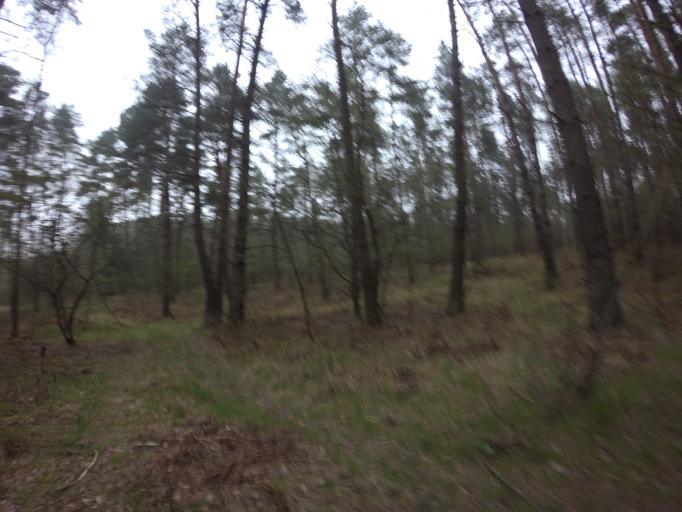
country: PL
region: West Pomeranian Voivodeship
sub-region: Powiat choszczenski
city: Recz
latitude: 53.1894
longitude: 15.5359
